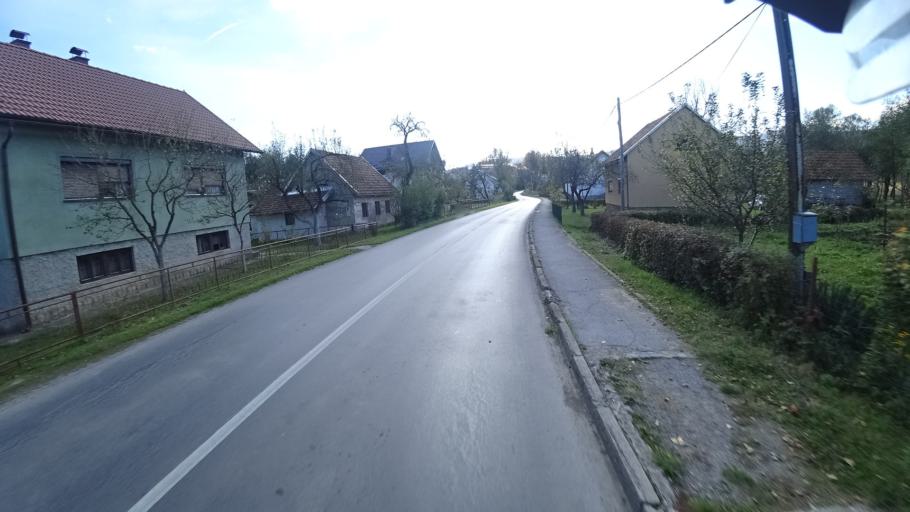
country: HR
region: Karlovacka
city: Plaski
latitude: 45.0865
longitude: 15.3665
